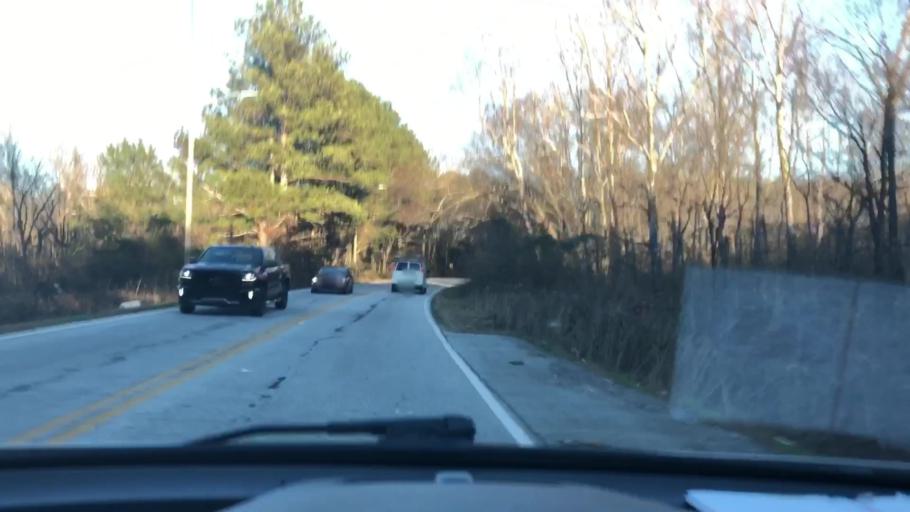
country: US
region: Georgia
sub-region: Rockdale County
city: Lakeview Estates
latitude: 33.7341
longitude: -84.0603
